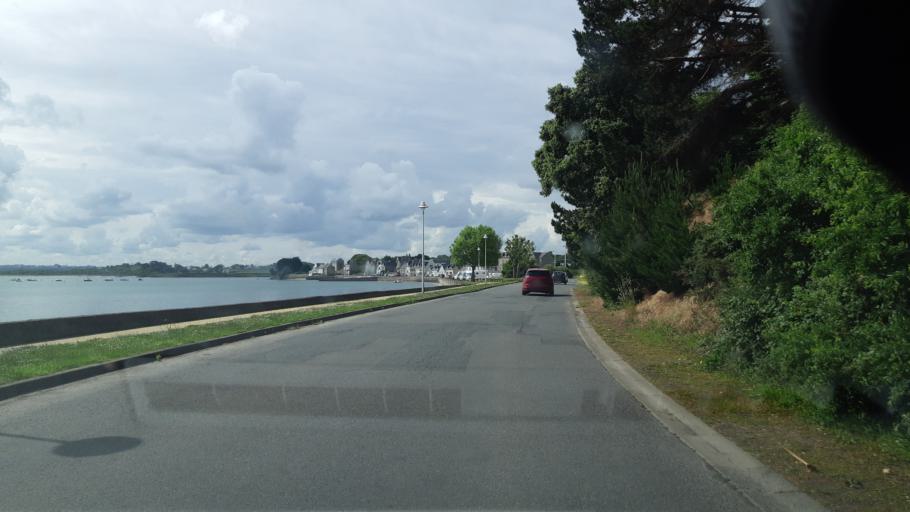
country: FR
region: Brittany
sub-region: Departement du Finistere
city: Saint-Pol-de-Leon
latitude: 48.6858
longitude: -3.9707
